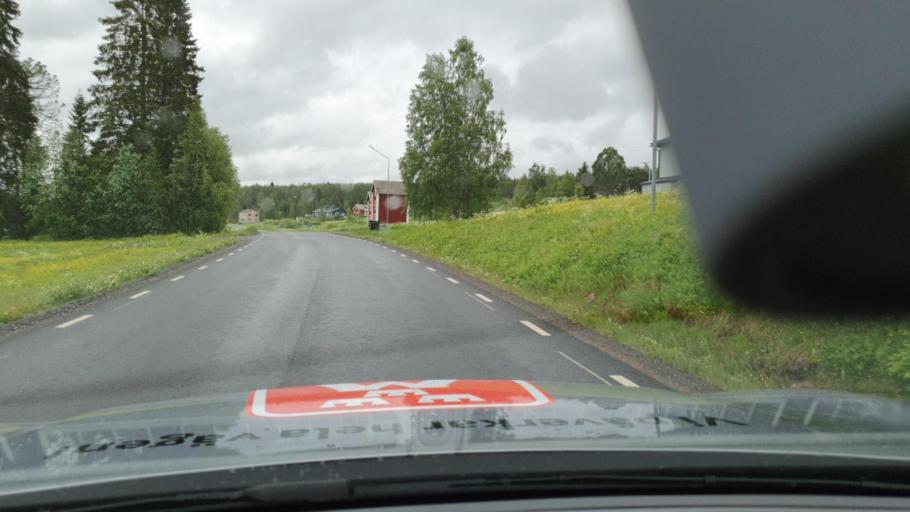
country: FI
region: Lapland
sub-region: Torniolaakso
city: Ylitornio
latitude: 66.1784
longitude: 23.7891
